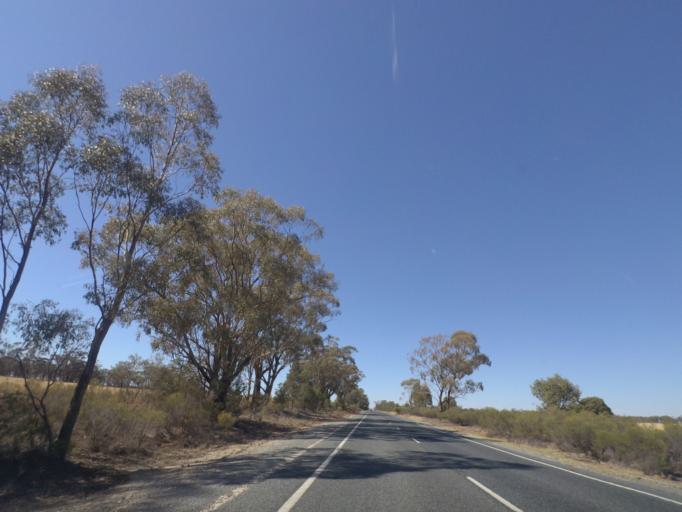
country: AU
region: New South Wales
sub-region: Bland
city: West Wyalong
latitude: -34.1604
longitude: 147.1169
